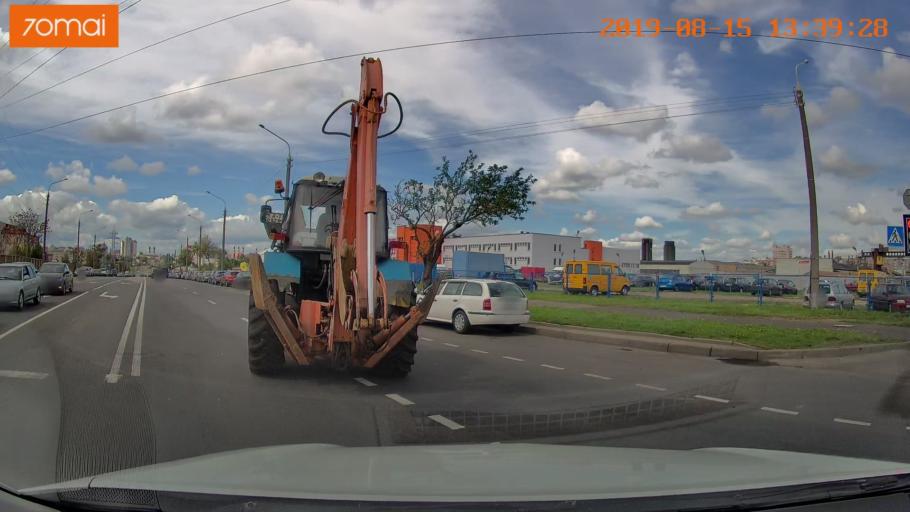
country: BY
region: Minsk
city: Minsk
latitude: 53.8775
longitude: 27.5928
